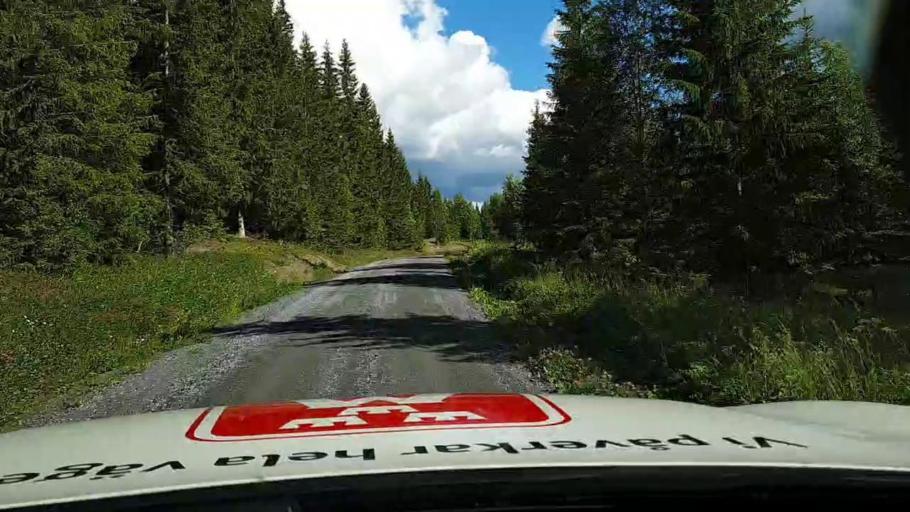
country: SE
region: Jaemtland
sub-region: Krokoms Kommun
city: Valla
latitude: 63.3176
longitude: 13.7702
